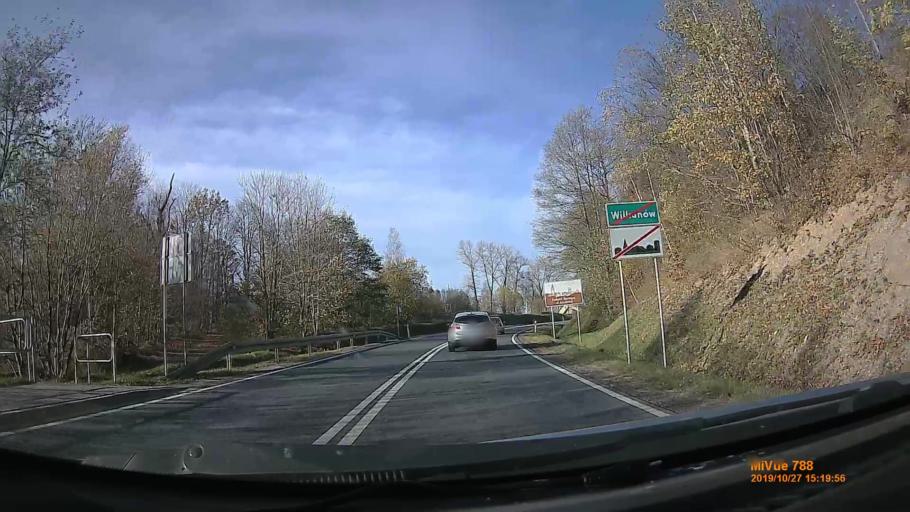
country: PL
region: Lower Silesian Voivodeship
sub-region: Powiat klodzki
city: Bystrzyca Klodzka
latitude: 50.2777
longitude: 16.6489
